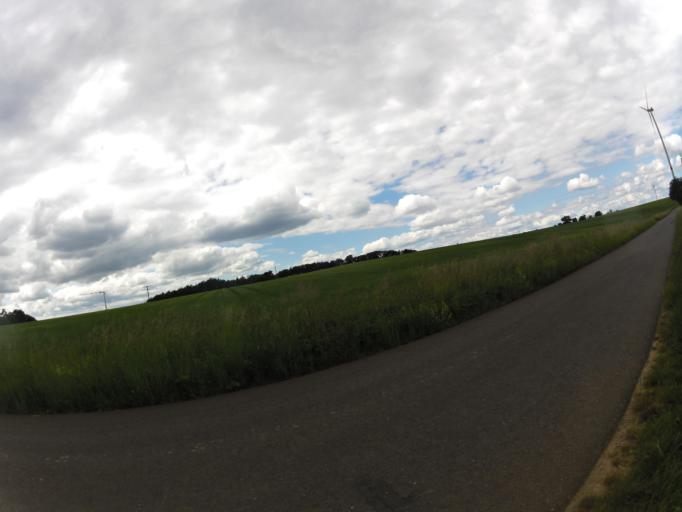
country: DE
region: Bavaria
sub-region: Regierungsbezirk Unterfranken
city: Guntersleben
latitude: 49.8756
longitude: 9.8775
